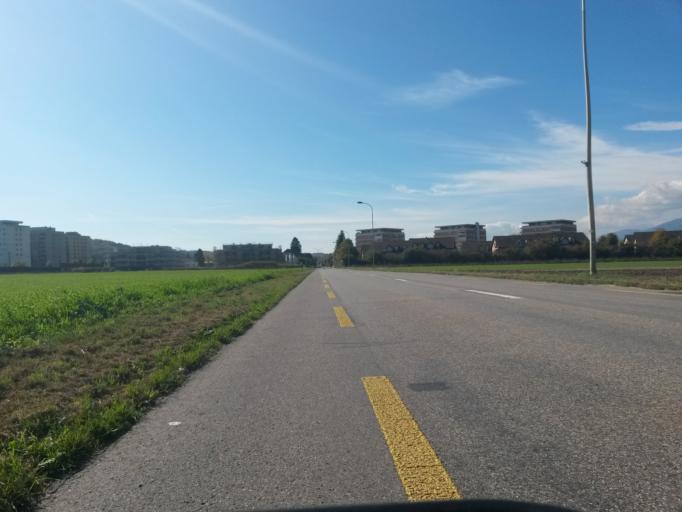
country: CH
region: Solothurn
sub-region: Bezirk Wasseramt
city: Zuchwil
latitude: 47.2118
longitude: 7.5674
